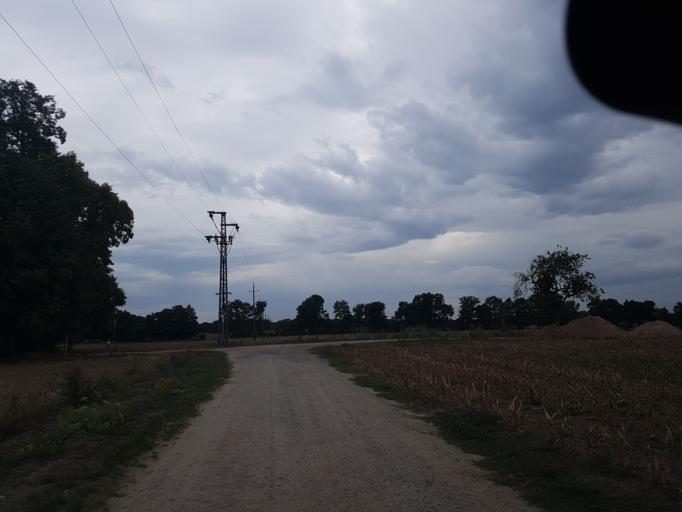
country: DE
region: Saxony-Anhalt
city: Lindau
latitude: 52.0264
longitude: 12.2334
